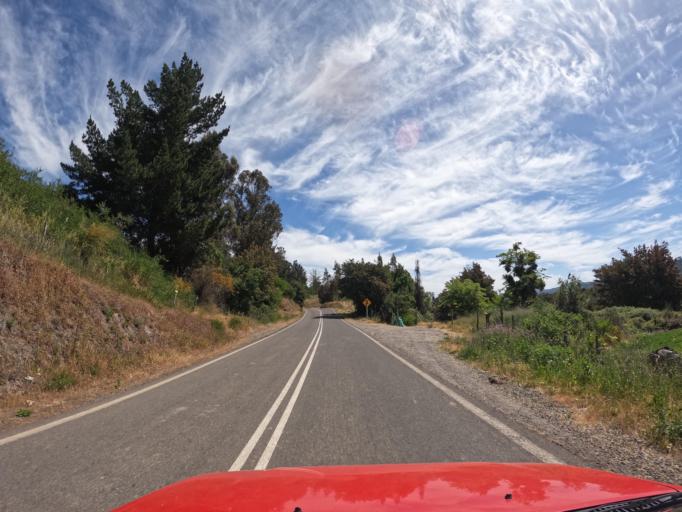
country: CL
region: Maule
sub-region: Provincia de Talca
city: Talca
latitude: -34.9909
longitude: -71.8503
